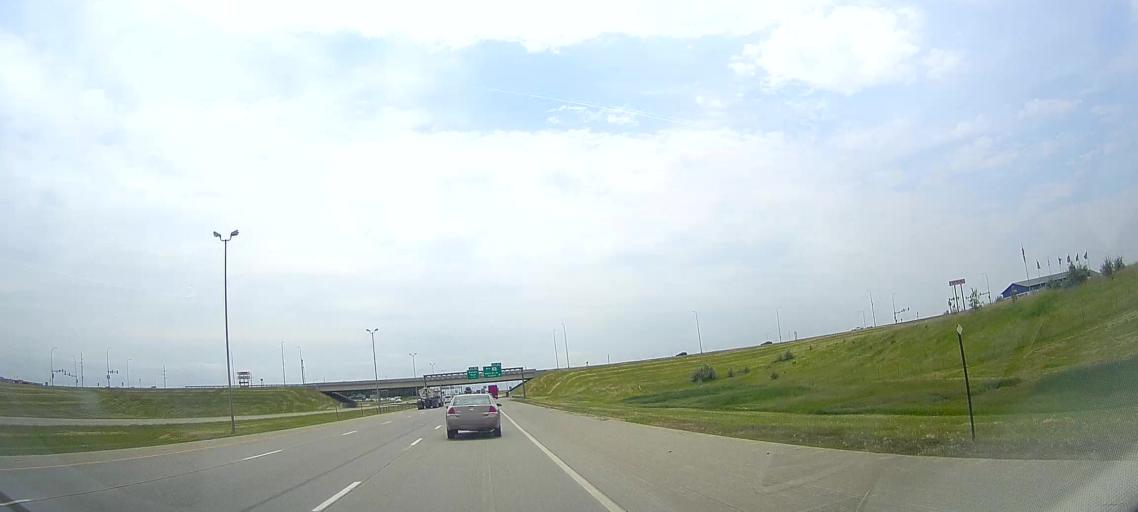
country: US
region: South Dakota
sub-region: Minnehaha County
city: Crooks
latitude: 43.6044
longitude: -96.7709
